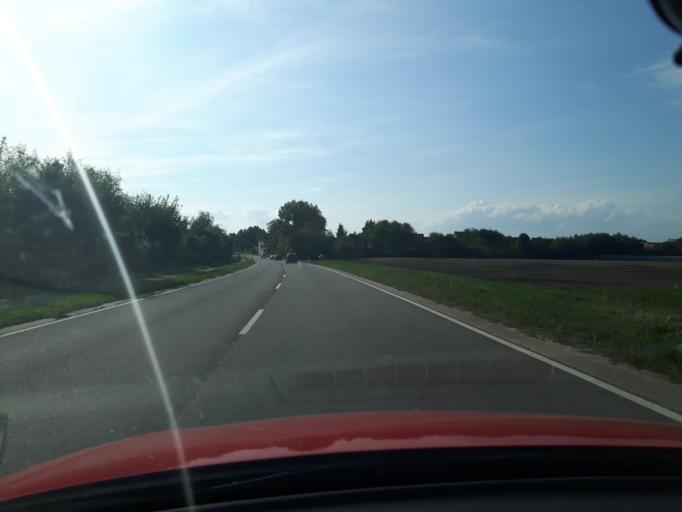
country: DE
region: Rheinland-Pfalz
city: Otterstadt
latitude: 49.3676
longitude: 8.4581
